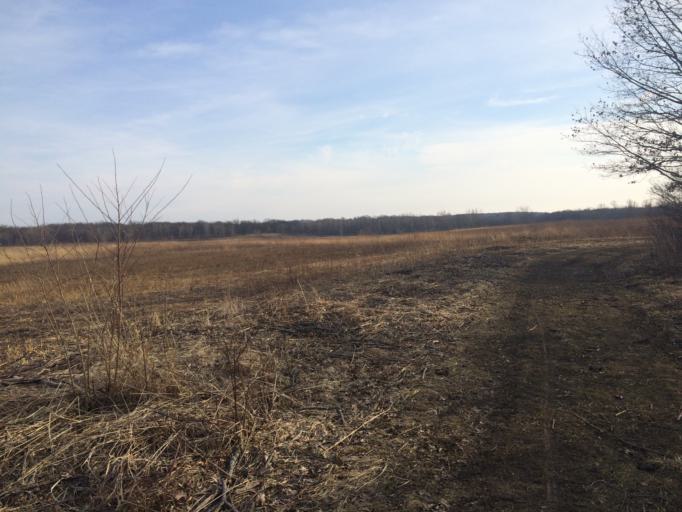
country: US
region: Illinois
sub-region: Cook County
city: Streamwood
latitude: 42.0577
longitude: -88.2042
